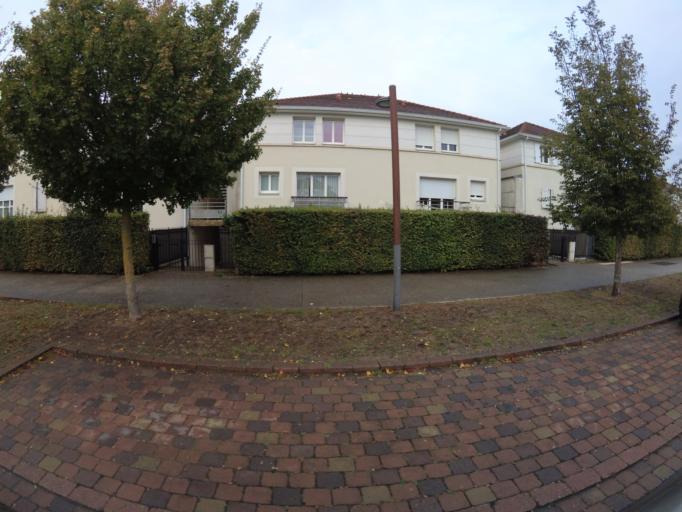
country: FR
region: Ile-de-France
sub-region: Departement de Seine-et-Marne
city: Chanteloup-en-Brie
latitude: 48.8595
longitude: 2.7419
